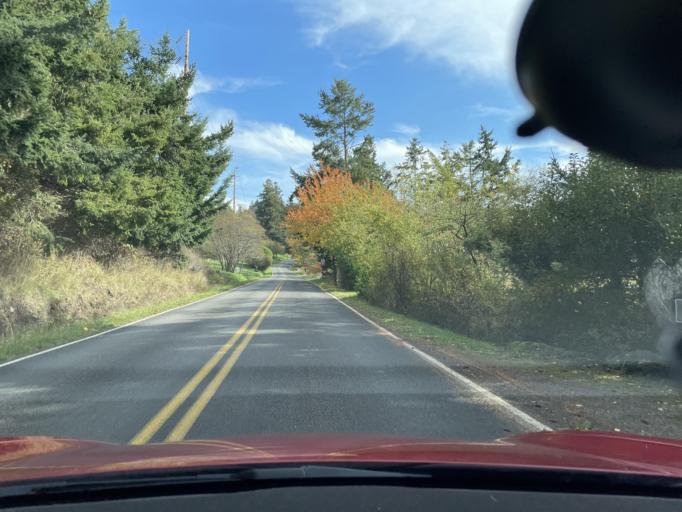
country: US
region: Washington
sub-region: San Juan County
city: Friday Harbor
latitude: 48.5202
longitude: -123.0019
